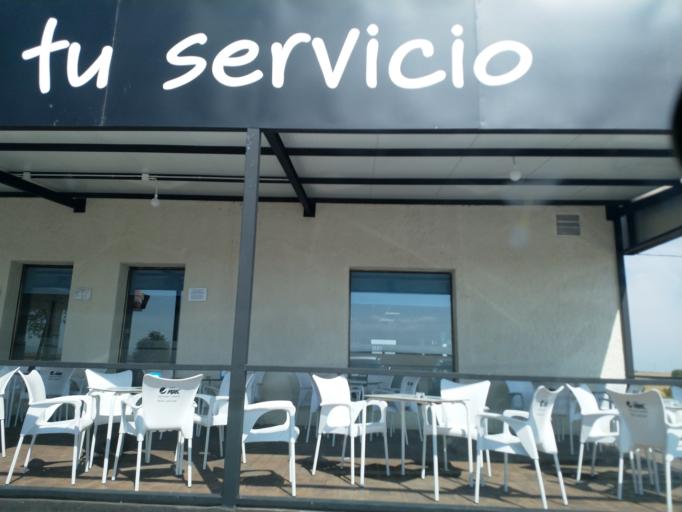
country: ES
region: Extremadura
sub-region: Provincia de Caceres
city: Berrocalejo
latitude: 39.8957
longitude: -5.3326
